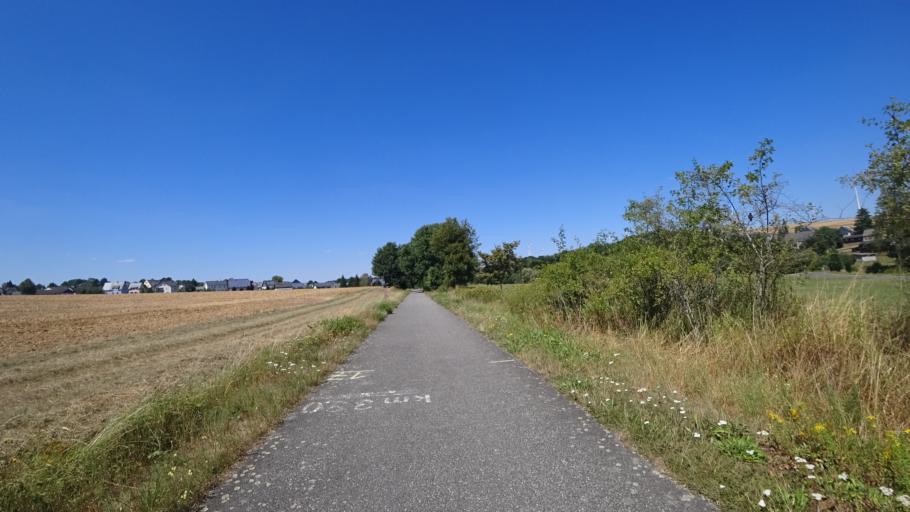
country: DE
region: Rheinland-Pfalz
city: Keidelheim
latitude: 50.0028
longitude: 7.4986
